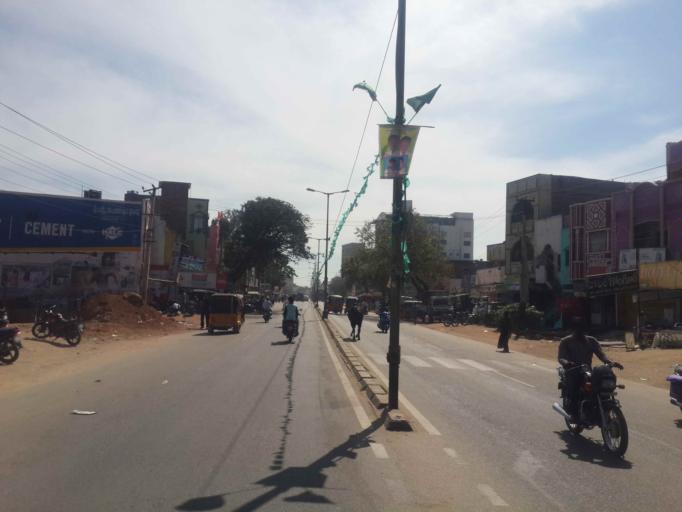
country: IN
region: Andhra Pradesh
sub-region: Anantapur
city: Kadiri
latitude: 14.1169
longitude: 78.1572
